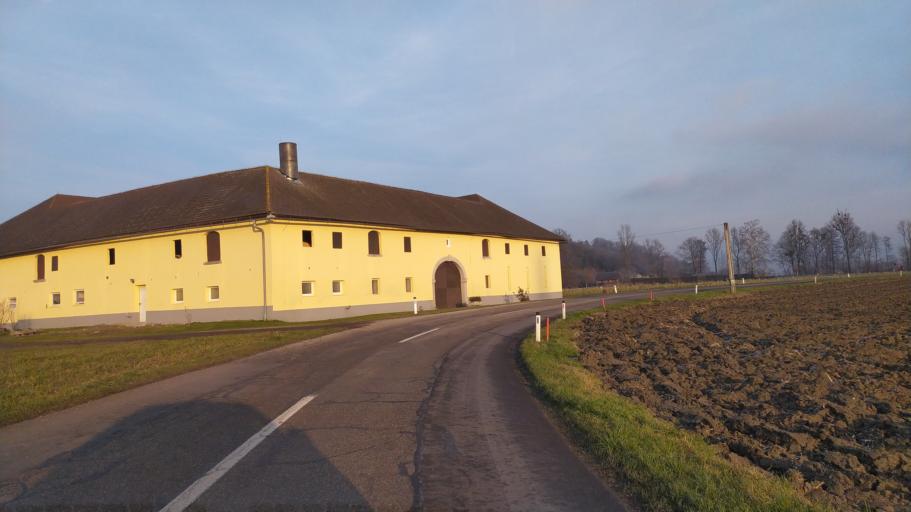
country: AT
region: Upper Austria
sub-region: Politischer Bezirk Urfahr-Umgebung
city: Goldworth
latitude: 48.3353
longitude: 14.1120
